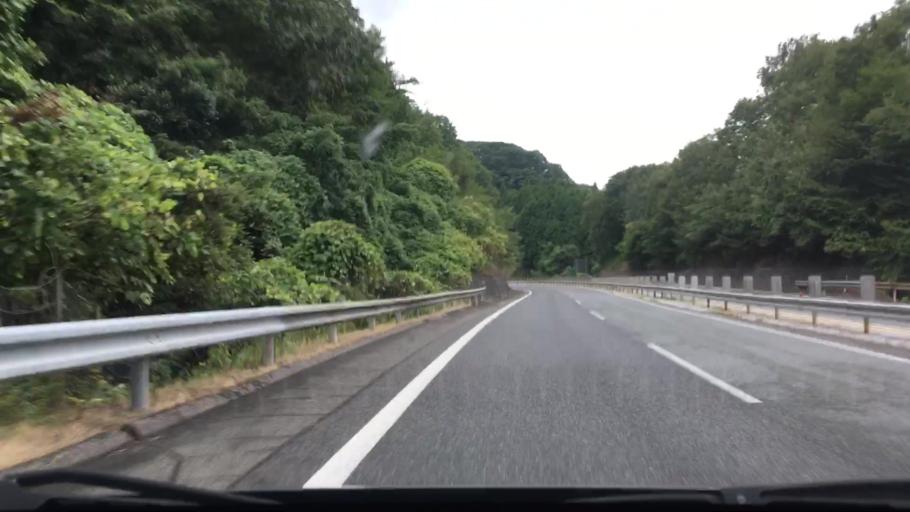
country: JP
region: Okayama
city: Niimi
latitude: 34.8975
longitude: 133.2933
